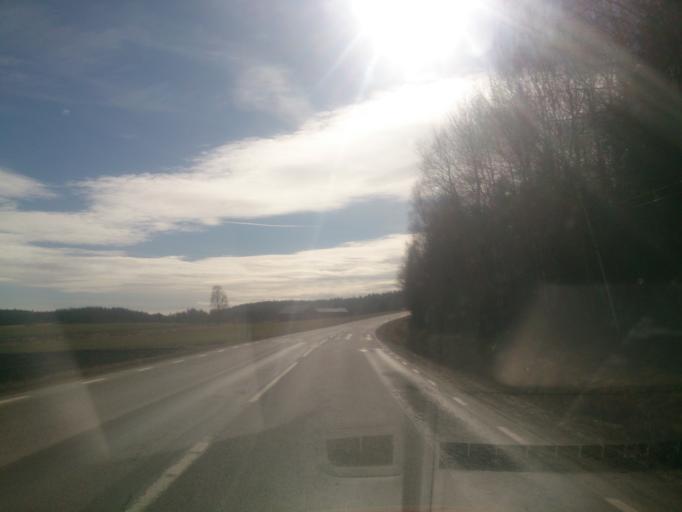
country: SE
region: OEstergoetland
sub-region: Finspangs Kommun
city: Finspang
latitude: 58.6453
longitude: 15.8207
